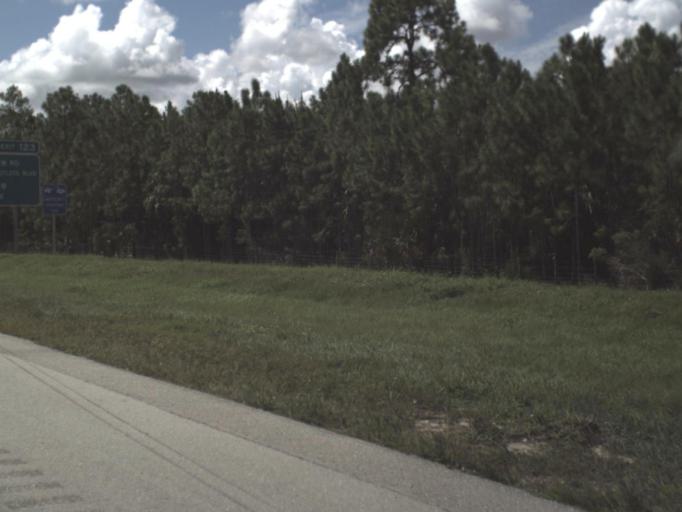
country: US
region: Florida
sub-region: Lee County
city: Estero
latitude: 26.4450
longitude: -81.7827
